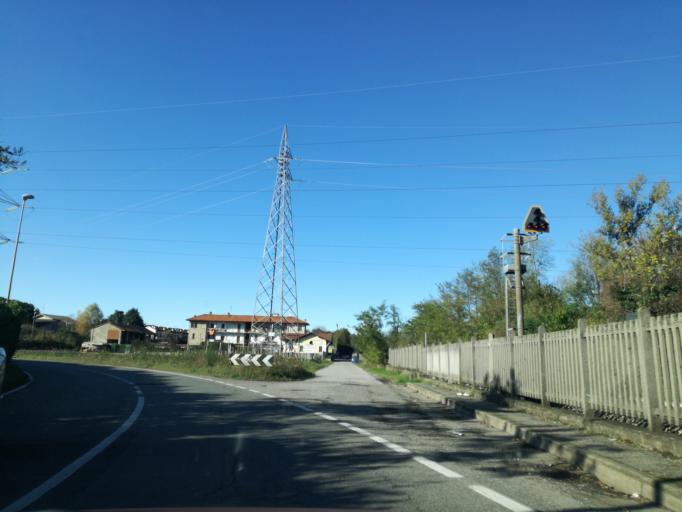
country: IT
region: Lombardy
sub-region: Provincia di Monza e Brianza
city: Lesmo
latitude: 45.6370
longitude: 9.2937
